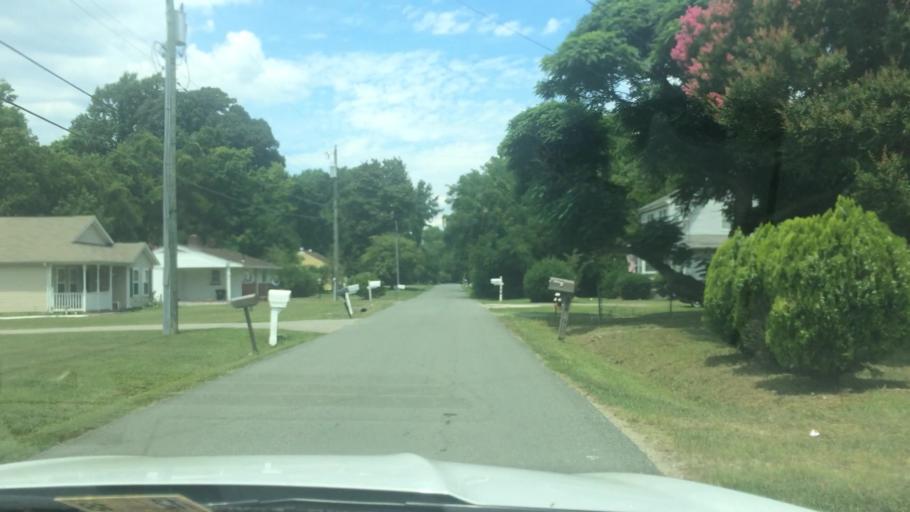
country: US
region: Virginia
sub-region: City of Williamsburg
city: Williamsburg
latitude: 37.2180
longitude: -76.6264
